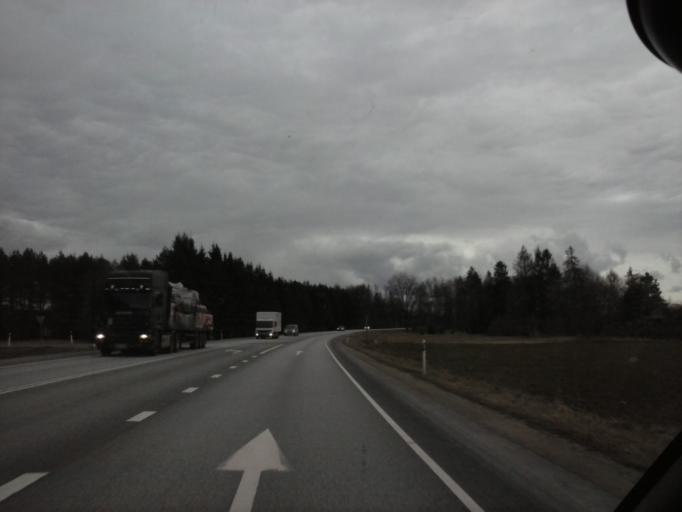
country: EE
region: Jaervamaa
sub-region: Paide linn
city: Paide
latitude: 58.8423
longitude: 25.7398
